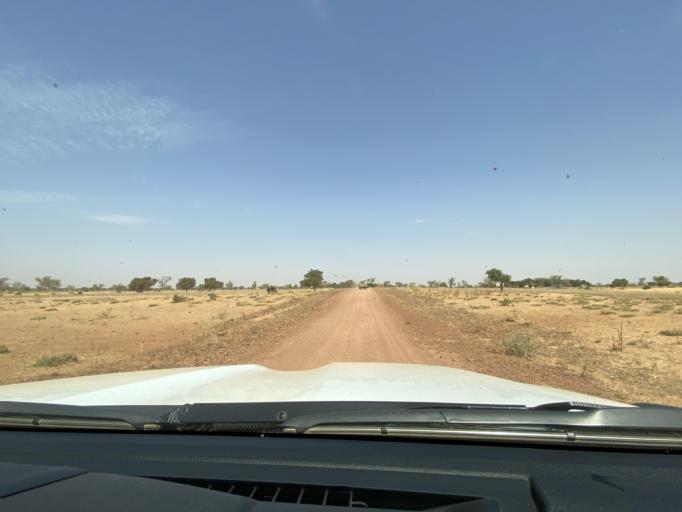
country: NE
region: Dosso
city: Birnin Gaoure
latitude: 13.2370
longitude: 2.8674
